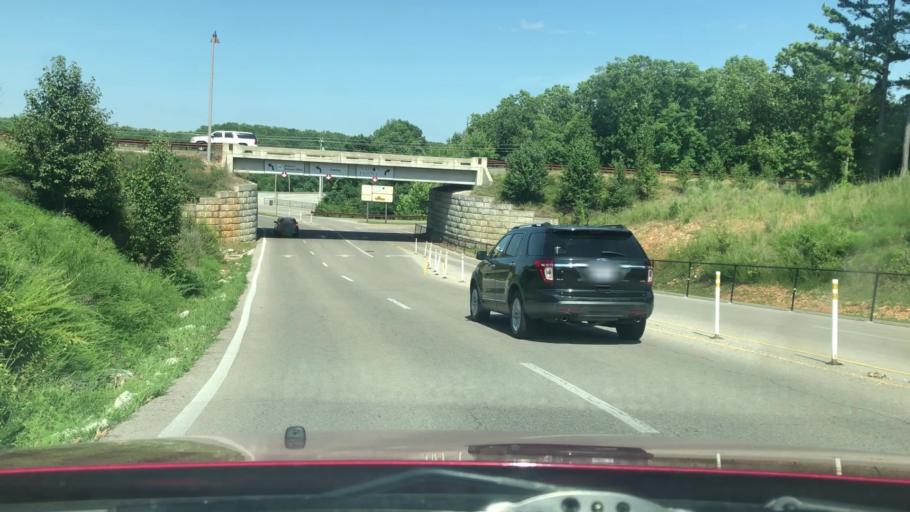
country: US
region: Missouri
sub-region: Stone County
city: Kimberling City
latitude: 36.6603
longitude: -93.3380
